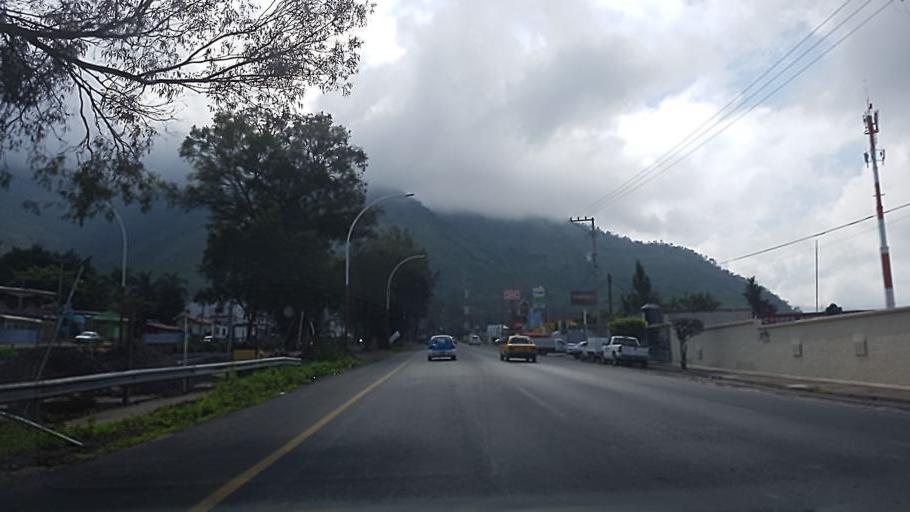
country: MX
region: Nayarit
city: Tepic
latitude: 21.5006
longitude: -104.9124
